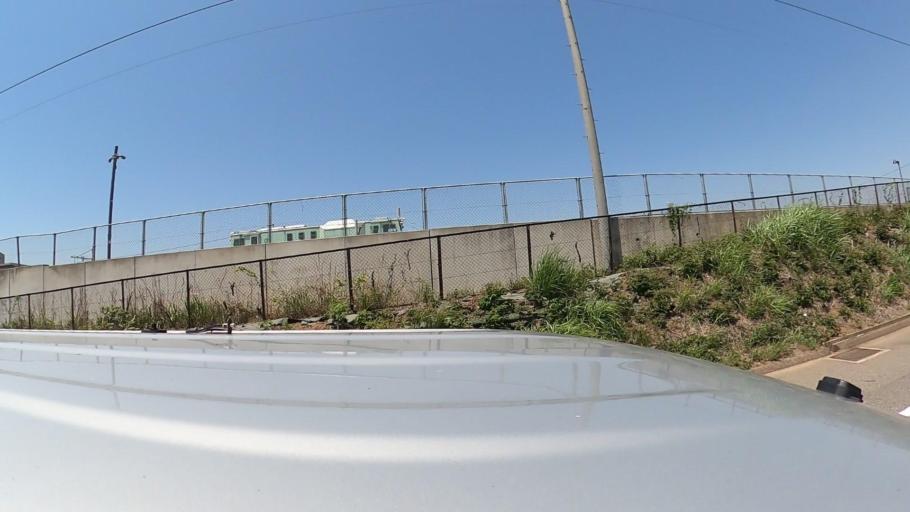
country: JP
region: Ibaraki
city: Mitsukaido
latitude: 35.9990
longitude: 140.0358
